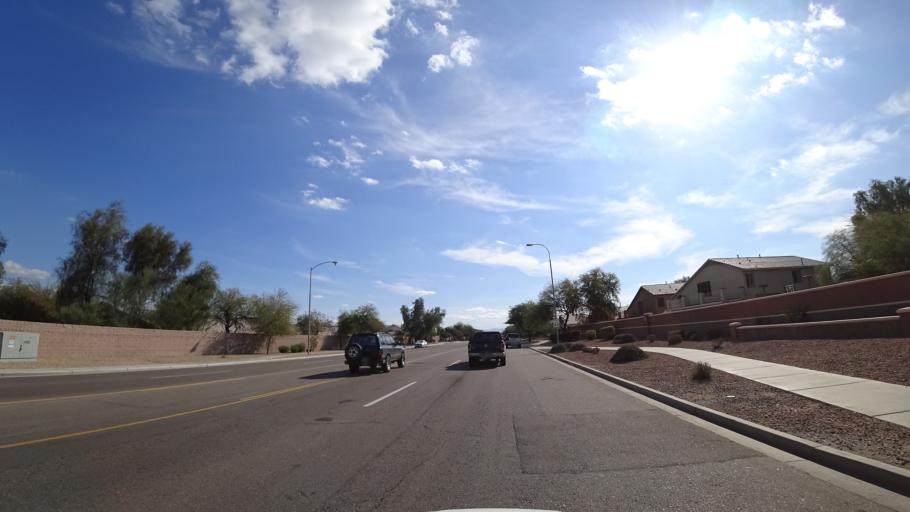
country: US
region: Arizona
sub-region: Maricopa County
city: Peoria
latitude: 33.6086
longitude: -112.2201
